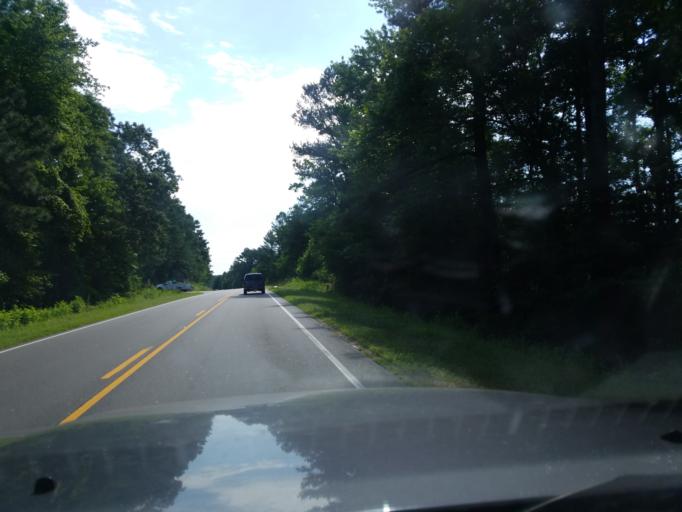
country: US
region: North Carolina
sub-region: Vance County
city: South Henderson
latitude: 36.3319
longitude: -78.4712
